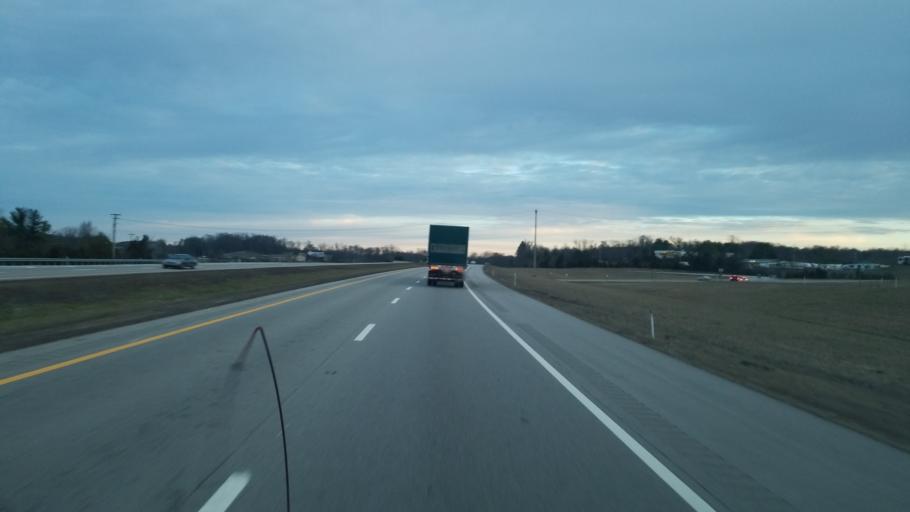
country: US
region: Tennessee
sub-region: Putnam County
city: Cookeville
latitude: 36.1003
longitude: -85.5043
